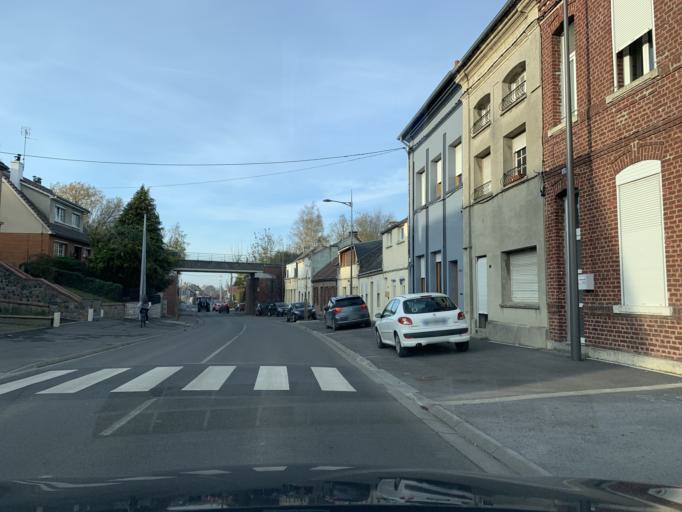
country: FR
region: Nord-Pas-de-Calais
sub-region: Departement du Nord
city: Cambrai
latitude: 50.1604
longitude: 3.2509
